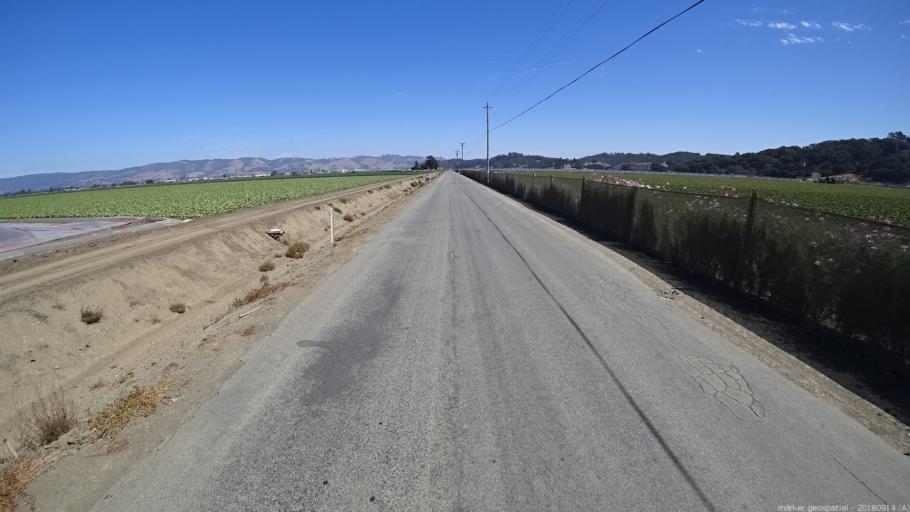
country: US
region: California
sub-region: Monterey County
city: Pajaro
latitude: 36.8833
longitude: -121.7610
